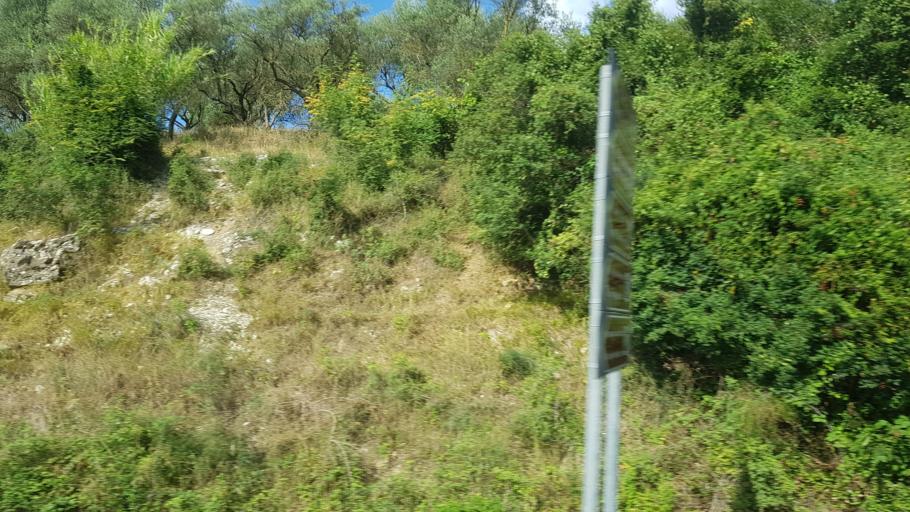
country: AL
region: Vlore
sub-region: Rrethi i Delvines
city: Mesopotam
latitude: 39.9020
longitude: 20.0856
